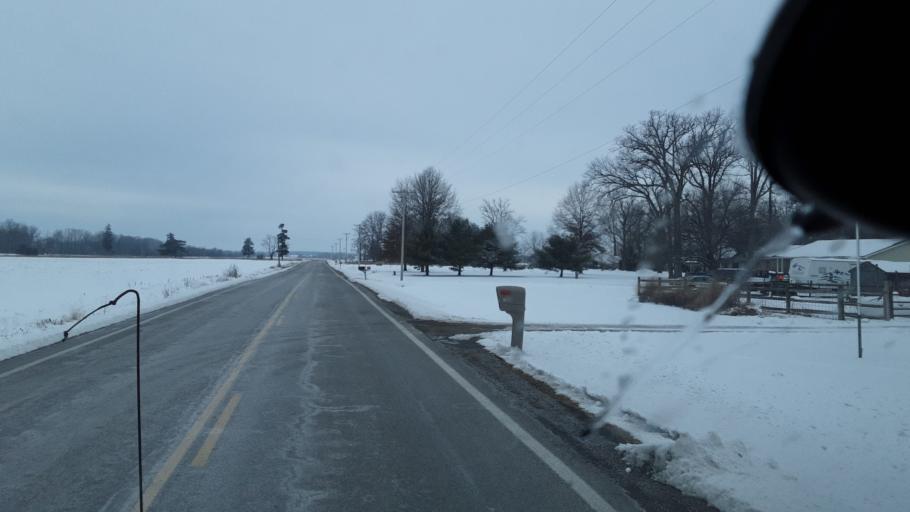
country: US
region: Ohio
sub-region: Champaign County
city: Mechanicsburg
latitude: 40.1195
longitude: -83.4642
